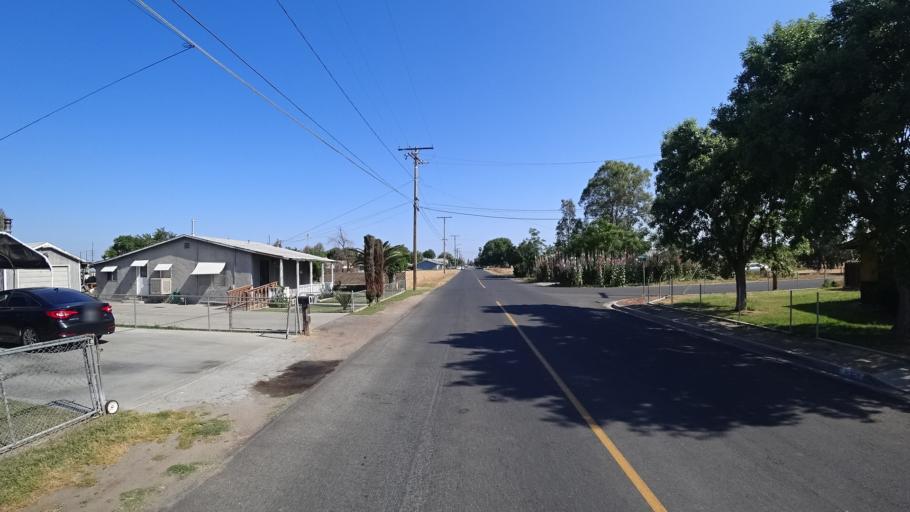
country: US
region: California
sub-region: Kings County
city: Home Garden
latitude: 36.3081
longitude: -119.6527
